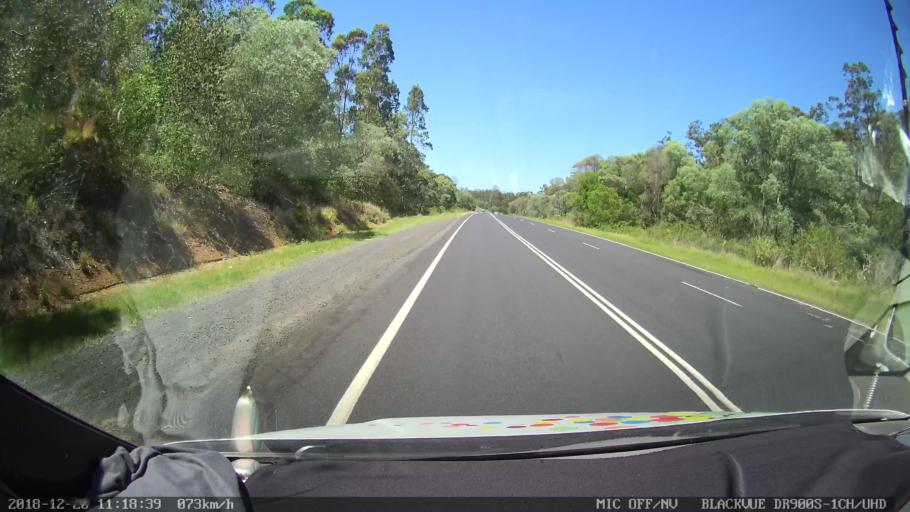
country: AU
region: New South Wales
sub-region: Richmond Valley
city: Casino
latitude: -29.0539
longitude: 153.0062
